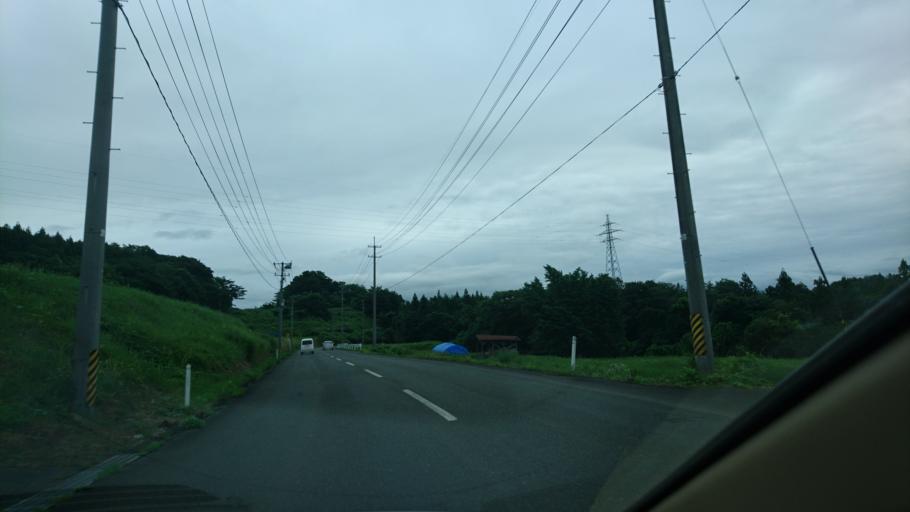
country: JP
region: Iwate
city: Mizusawa
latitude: 39.1964
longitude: 141.1962
